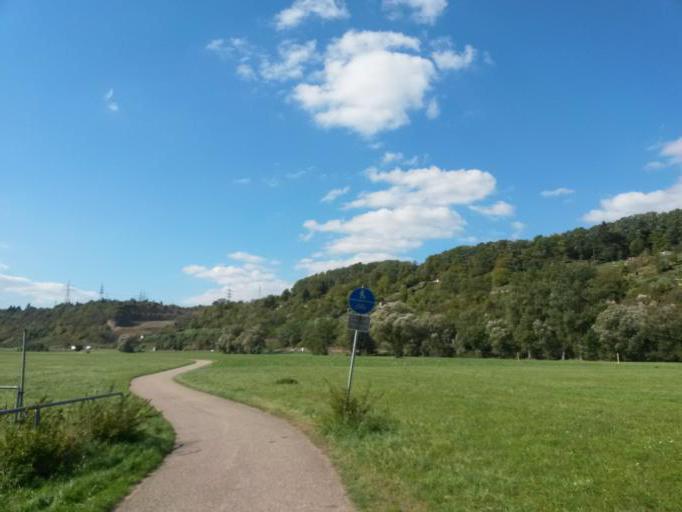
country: DE
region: Baden-Wuerttemberg
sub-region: Karlsruhe Region
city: Muhlacker
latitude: 48.9466
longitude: 8.8262
